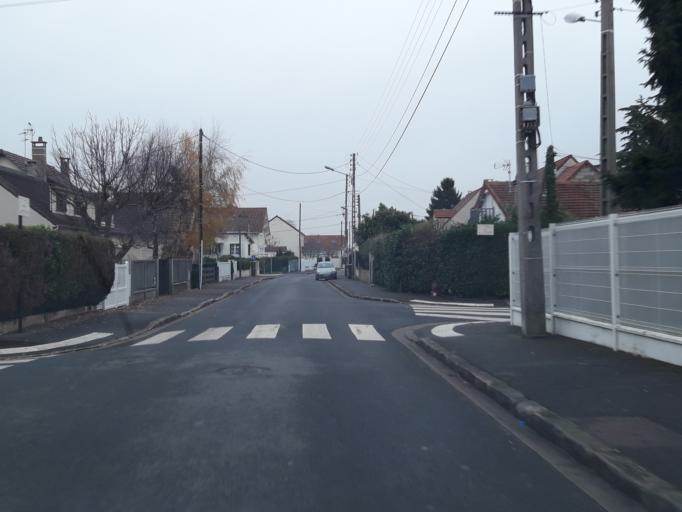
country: FR
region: Ile-de-France
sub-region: Departement de l'Essonne
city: Morsang-sur-Orge
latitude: 48.6587
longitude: 2.3513
